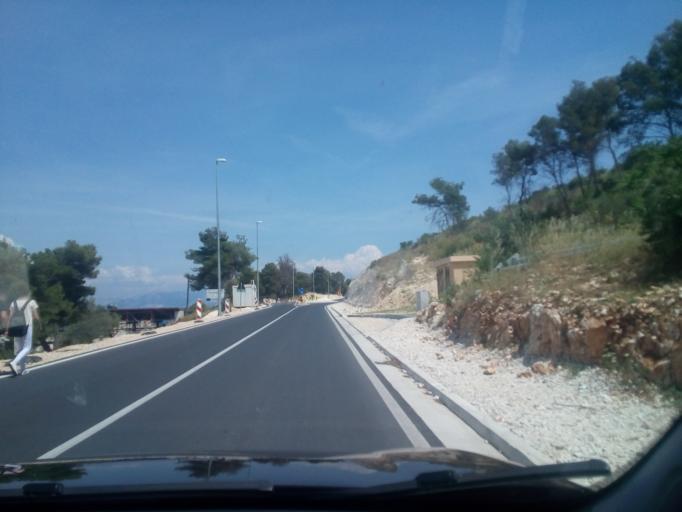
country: HR
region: Splitsko-Dalmatinska
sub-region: Grad Trogir
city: Trogir
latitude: 43.5165
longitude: 16.2636
